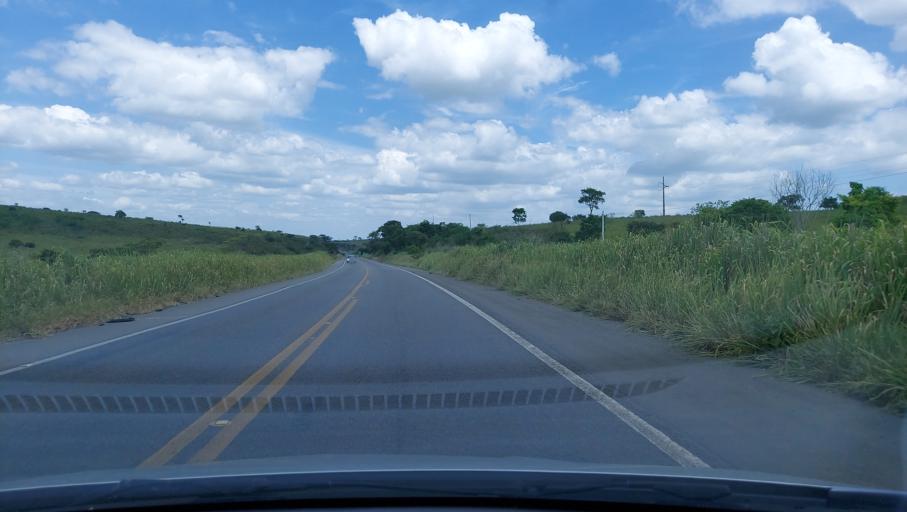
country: BR
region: Bahia
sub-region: Andarai
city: Vera Cruz
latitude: -12.4645
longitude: -40.9053
